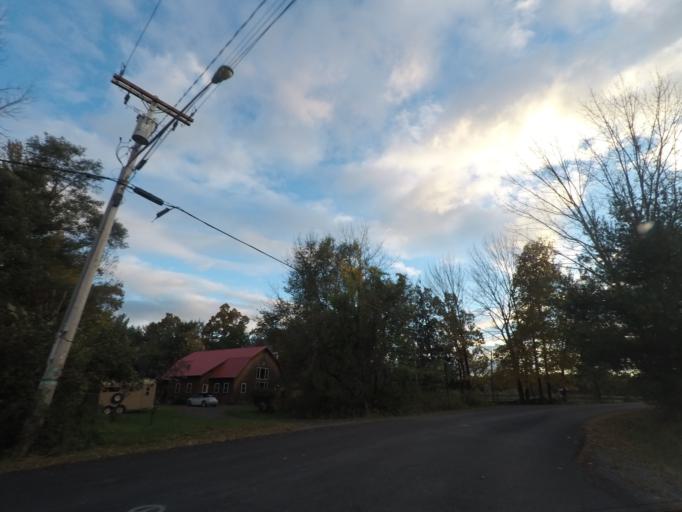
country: US
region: New York
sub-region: Rensselaer County
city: Nassau
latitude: 42.5358
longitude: -73.5750
